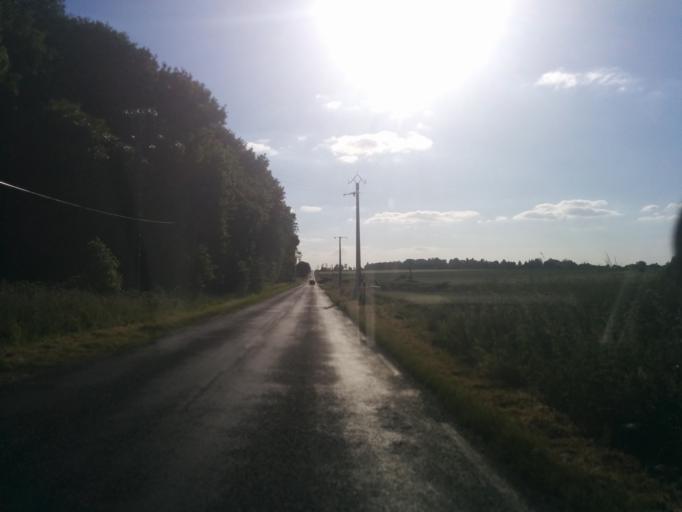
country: FR
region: Haute-Normandie
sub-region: Departement de l'Eure
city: Gasny
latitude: 49.0950
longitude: 1.5739
